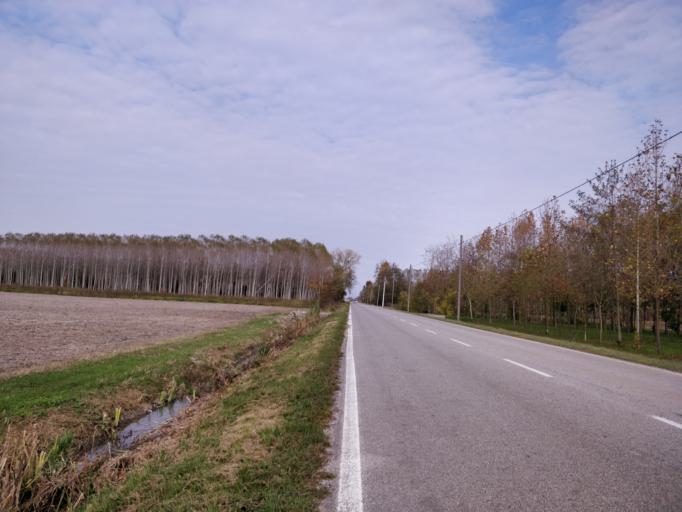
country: IT
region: Friuli Venezia Giulia
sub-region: Provincia di Udine
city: Bertiolo
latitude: 45.9198
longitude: 13.0480
